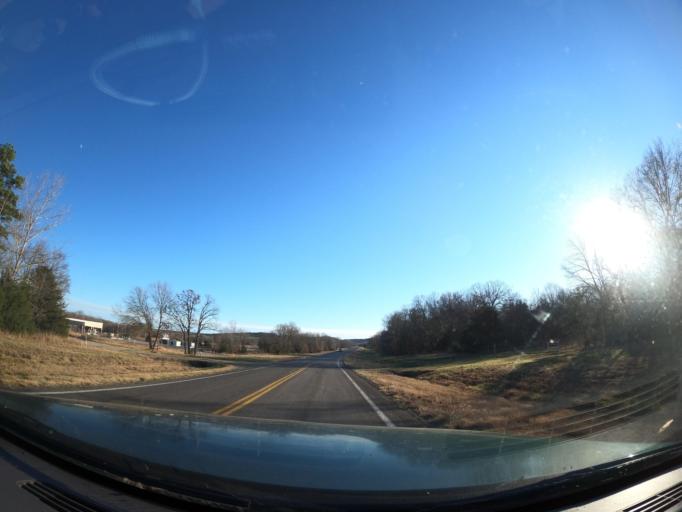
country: US
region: Oklahoma
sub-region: Latimer County
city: Wilburton
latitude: 34.9495
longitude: -95.3415
